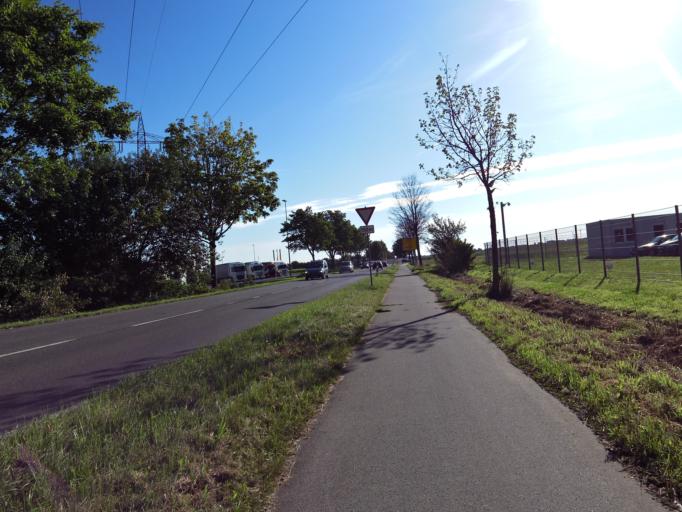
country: DE
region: North Rhine-Westphalia
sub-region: Regierungsbezirk Koln
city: Alsdorf
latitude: 50.8757
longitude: 6.1896
